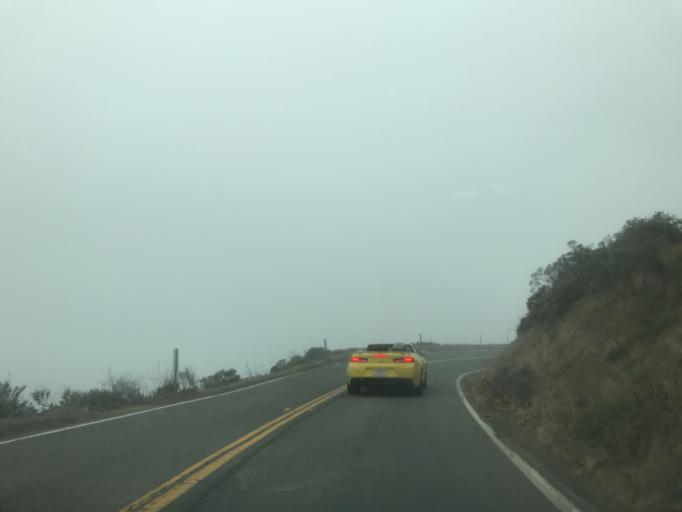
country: US
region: California
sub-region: Sonoma County
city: Monte Rio
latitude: 38.4726
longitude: -123.1576
